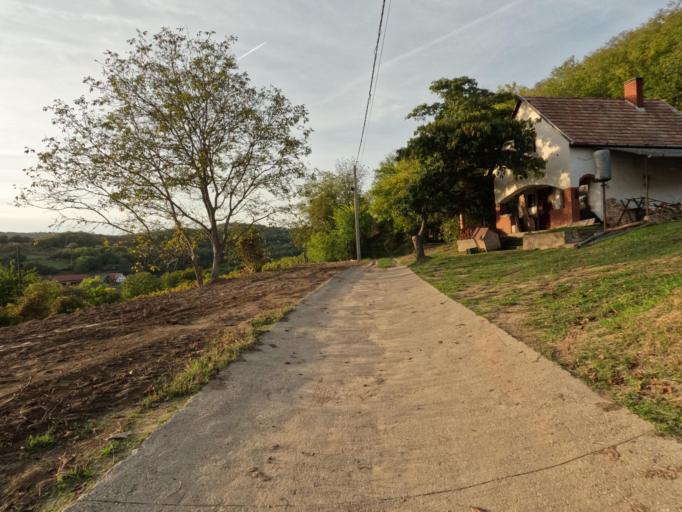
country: HU
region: Tolna
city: Szekszard
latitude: 46.3379
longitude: 18.6731
